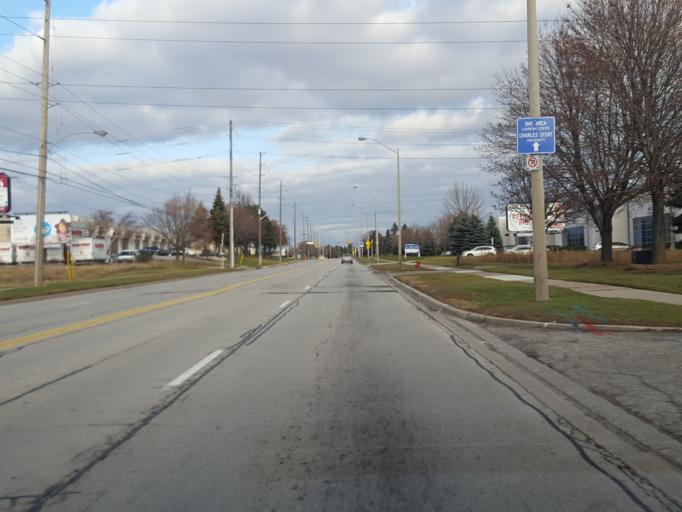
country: CA
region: Ontario
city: Burlington
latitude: 43.3548
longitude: -79.7955
